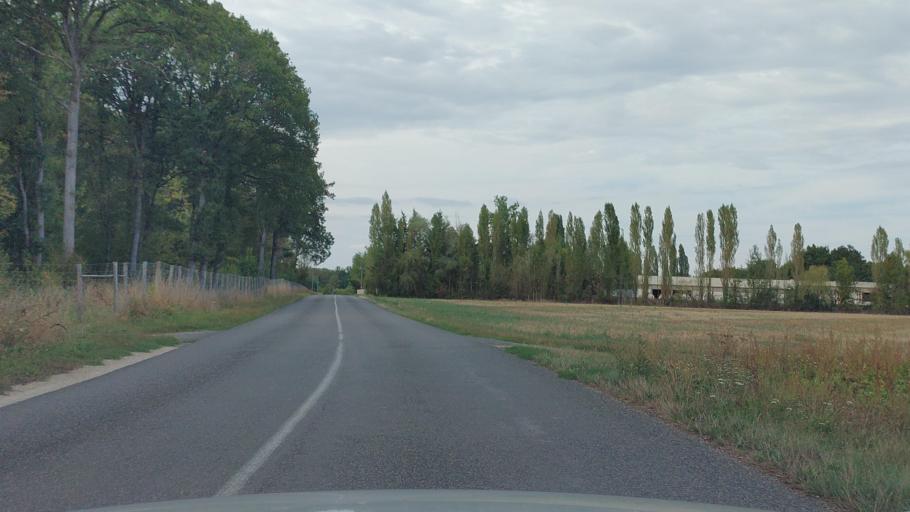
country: FR
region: Ile-de-France
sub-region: Departement de Seine-et-Marne
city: La Chapelle-Gauthier
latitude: 48.5500
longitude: 2.8766
